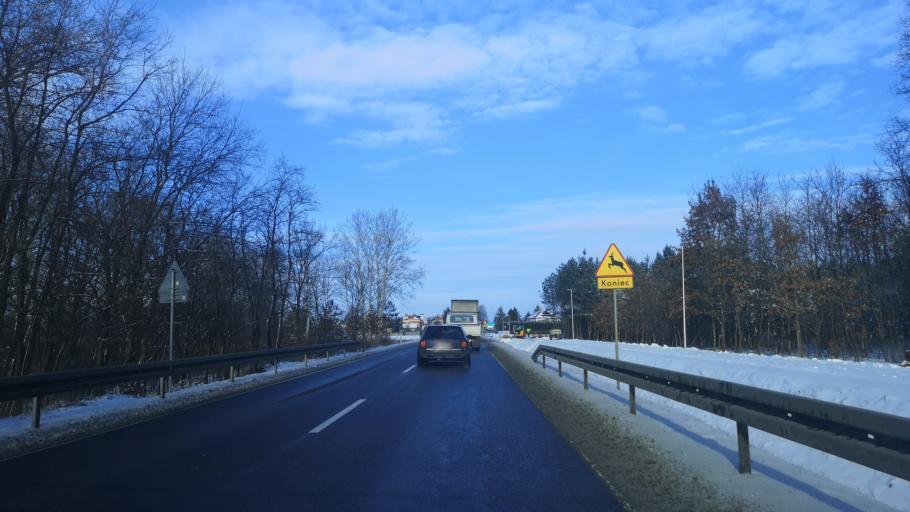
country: PL
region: Subcarpathian Voivodeship
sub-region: Powiat przeworski
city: Tryncza
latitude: 50.1318
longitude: 22.5366
